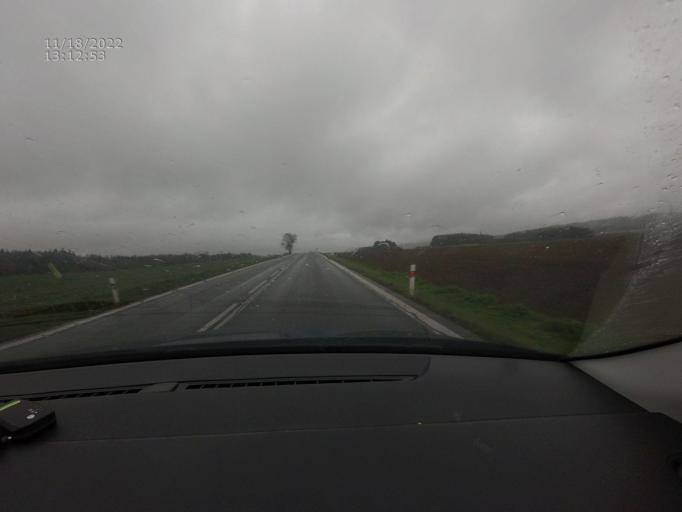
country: CZ
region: Plzensky
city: Horazd'ovice
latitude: 49.3248
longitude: 13.6149
